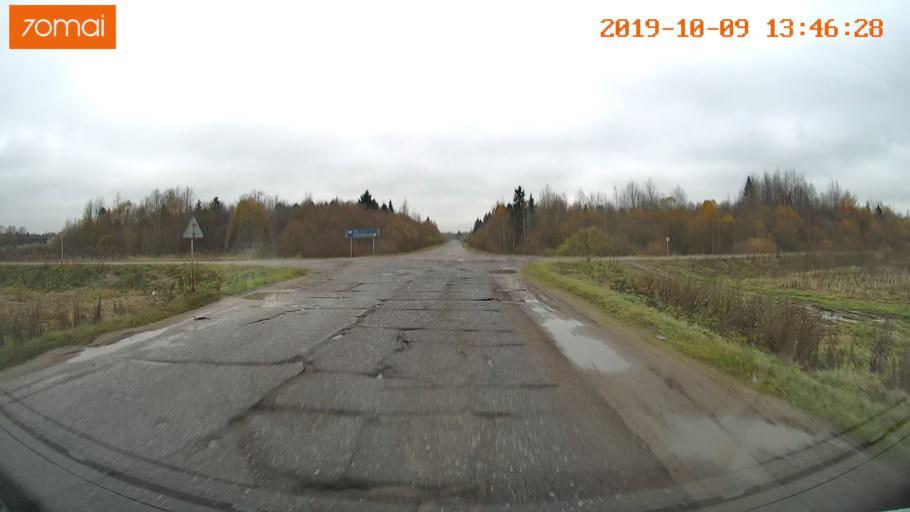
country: RU
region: Kostroma
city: Buy
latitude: 58.3841
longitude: 41.2183
